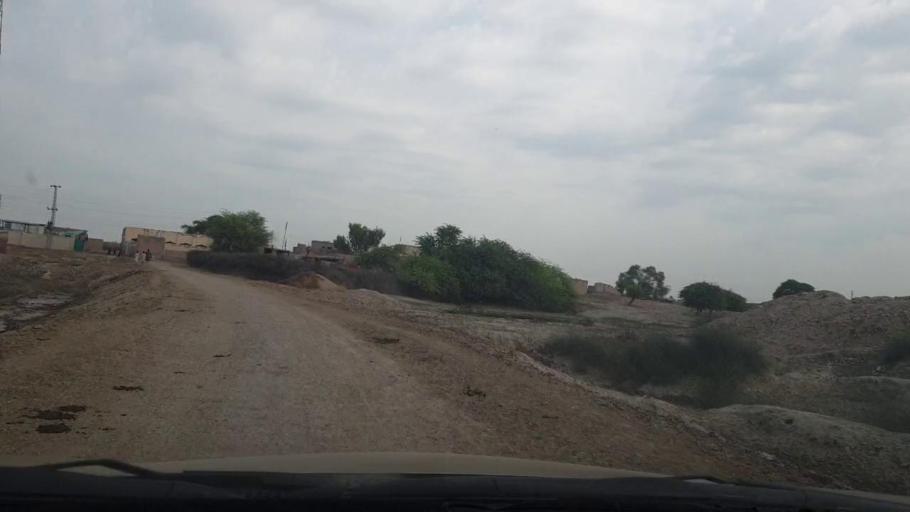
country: PK
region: Sindh
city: Ratodero
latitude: 27.7011
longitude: 68.2298
